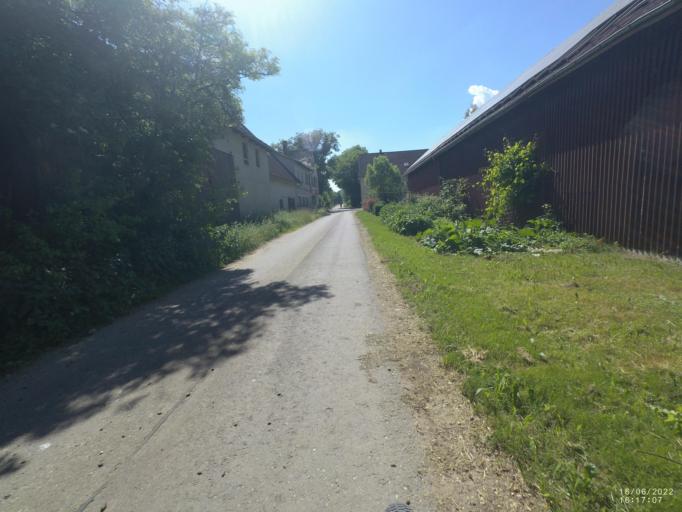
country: DE
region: Baden-Wuerttemberg
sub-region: Regierungsbezirk Stuttgart
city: Gerstetten
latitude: 48.6226
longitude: 10.0774
